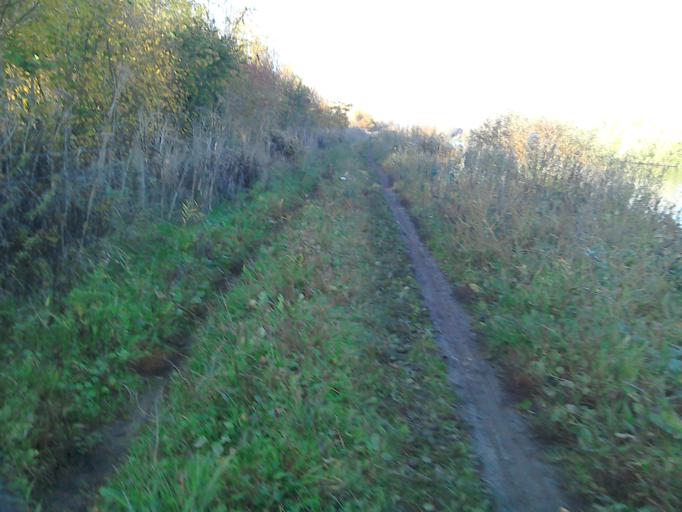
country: GB
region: England
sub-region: Oxfordshire
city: Radley
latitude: 51.6969
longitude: -1.2294
